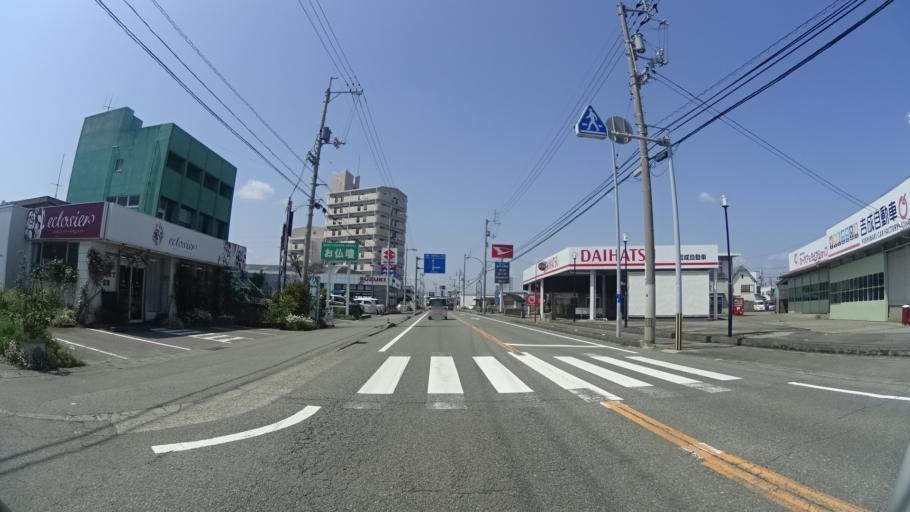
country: JP
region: Tokushima
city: Narutocho-mitsuishi
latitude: 34.1630
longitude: 134.5950
